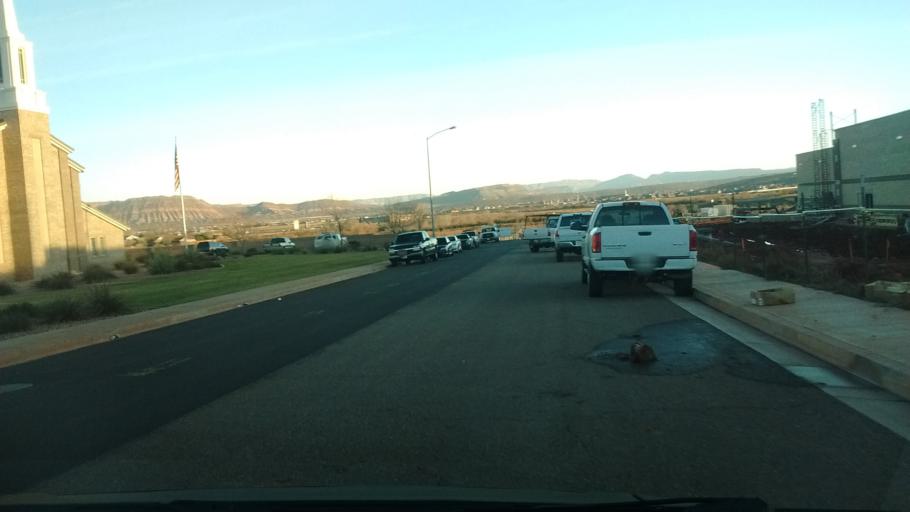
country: US
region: Utah
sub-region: Washington County
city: Washington
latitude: 37.1008
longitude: -113.5336
